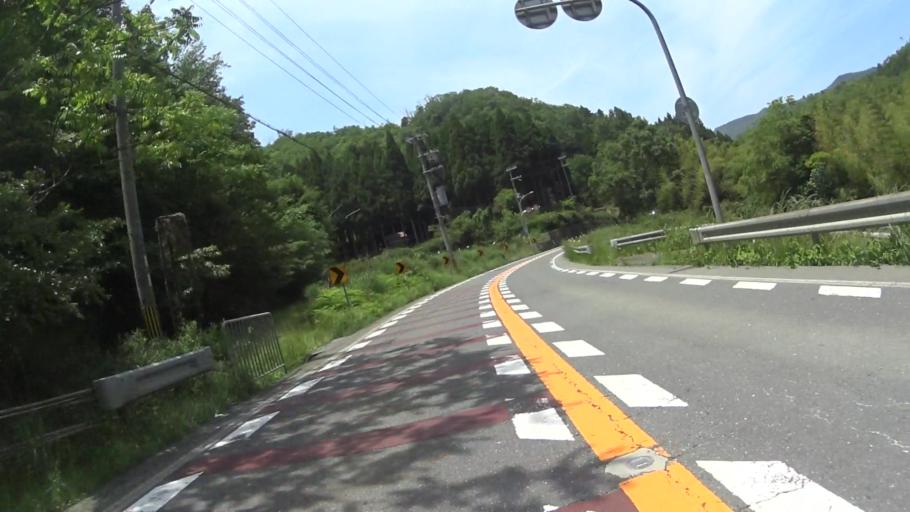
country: JP
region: Kyoto
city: Ayabe
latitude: 35.1969
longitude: 135.2839
